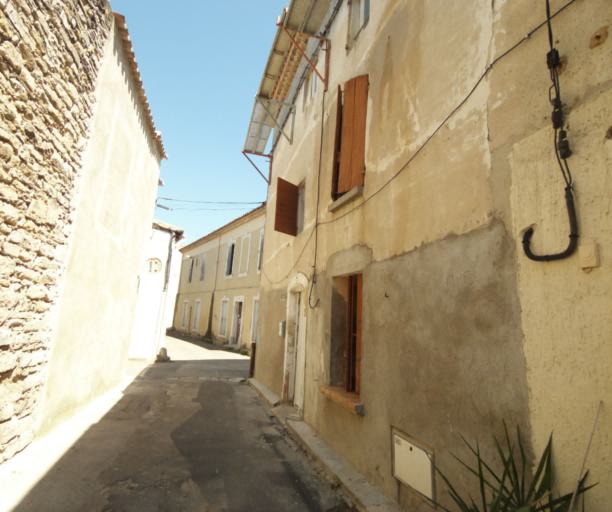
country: FR
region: Languedoc-Roussillon
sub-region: Departement de l'Herault
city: Marsillargues
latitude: 43.6659
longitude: 4.1785
